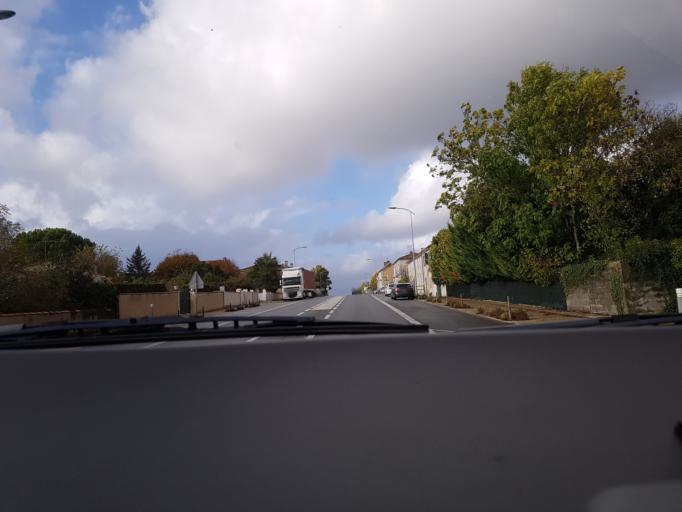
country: FR
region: Poitou-Charentes
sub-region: Departement de la Charente-Maritime
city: Les Gonds
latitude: 45.6522
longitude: -0.5869
